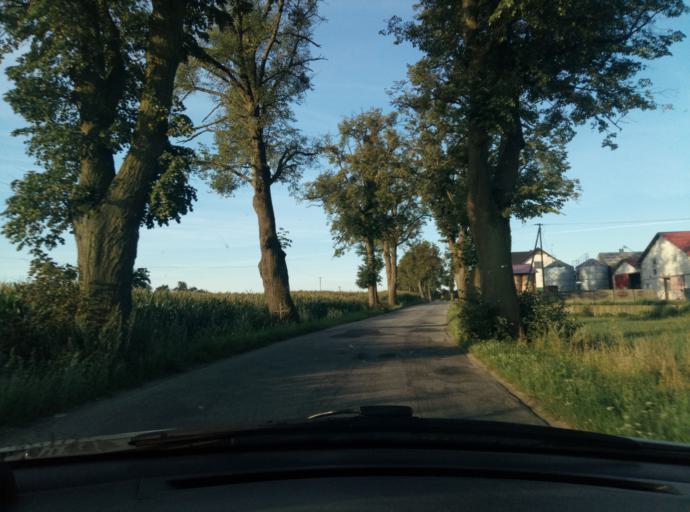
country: PL
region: Kujawsko-Pomorskie
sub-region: Powiat brodnicki
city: Jablonowo Pomorskie
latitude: 53.4194
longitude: 19.1816
